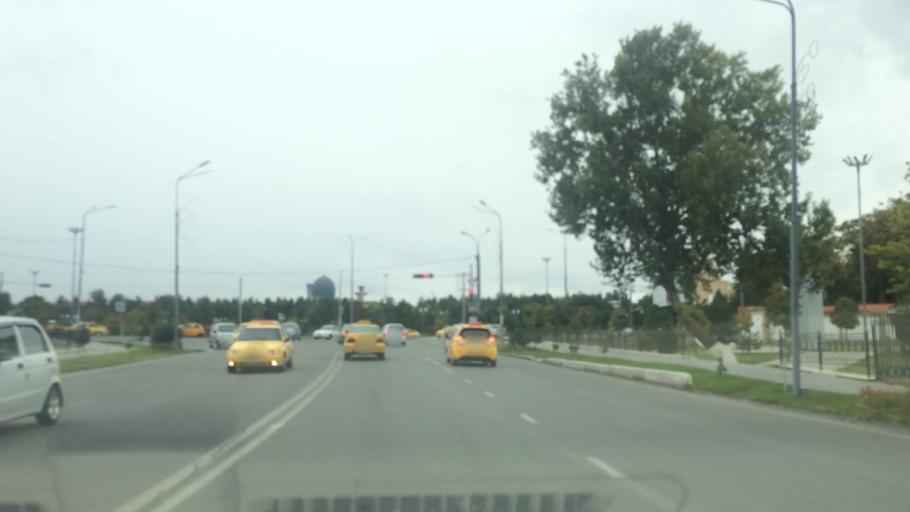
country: UZ
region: Samarqand
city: Samarqand
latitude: 39.6531
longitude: 66.9702
